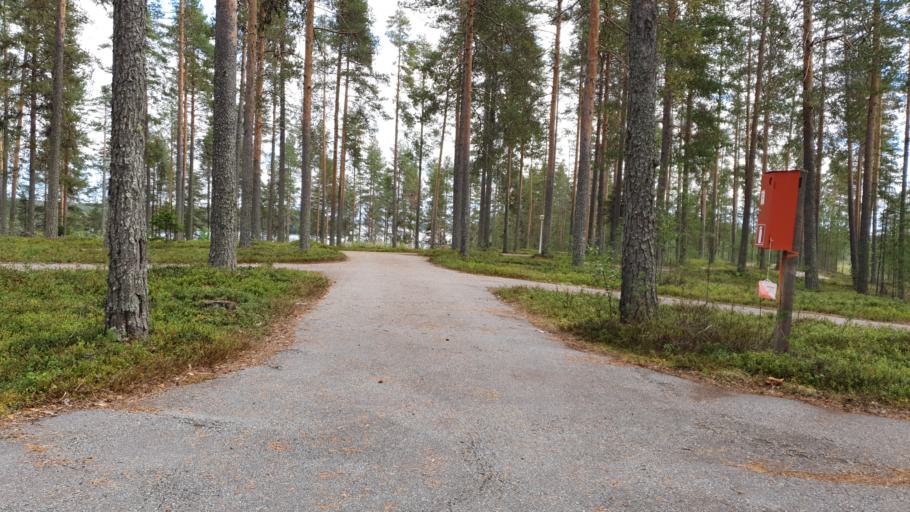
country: FI
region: Kainuu
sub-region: Kehys-Kainuu
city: Kuhmo
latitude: 64.1154
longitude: 29.5901
